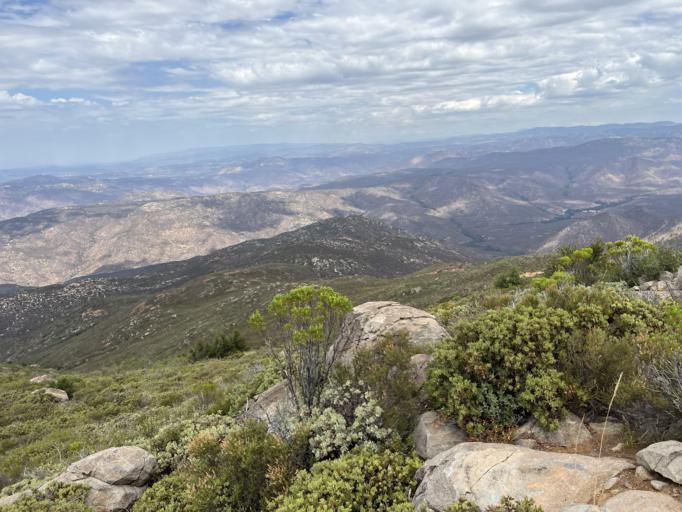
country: US
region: California
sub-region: San Diego County
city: Alpine
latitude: 32.8615
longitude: -116.7261
